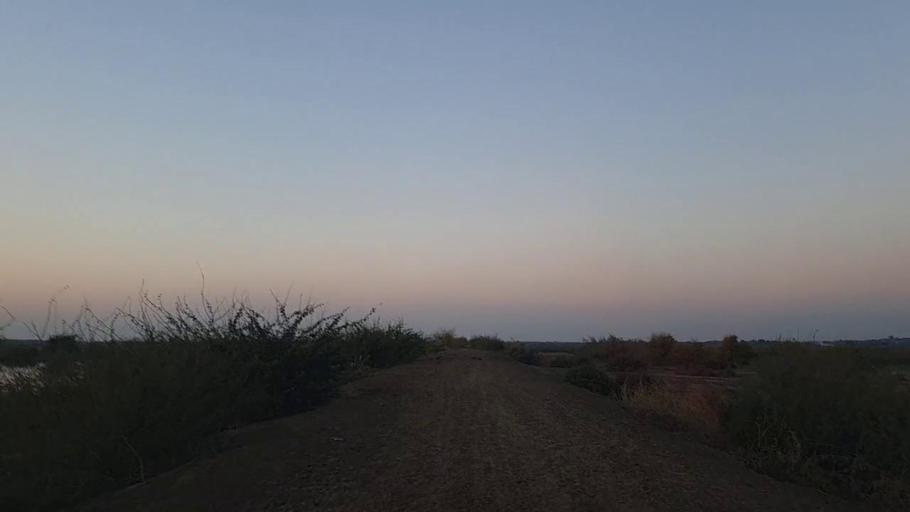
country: PK
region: Sindh
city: Tando Mittha Khan
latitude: 26.0740
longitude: 69.1548
